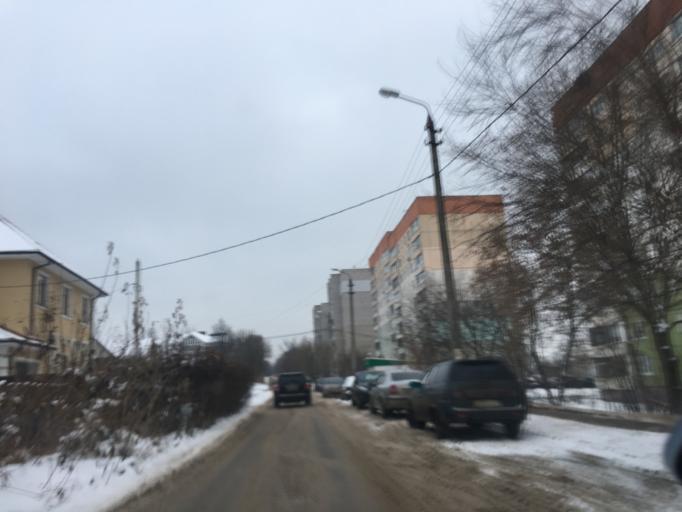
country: RU
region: Tula
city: Mendeleyevskiy
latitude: 54.1842
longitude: 37.5686
